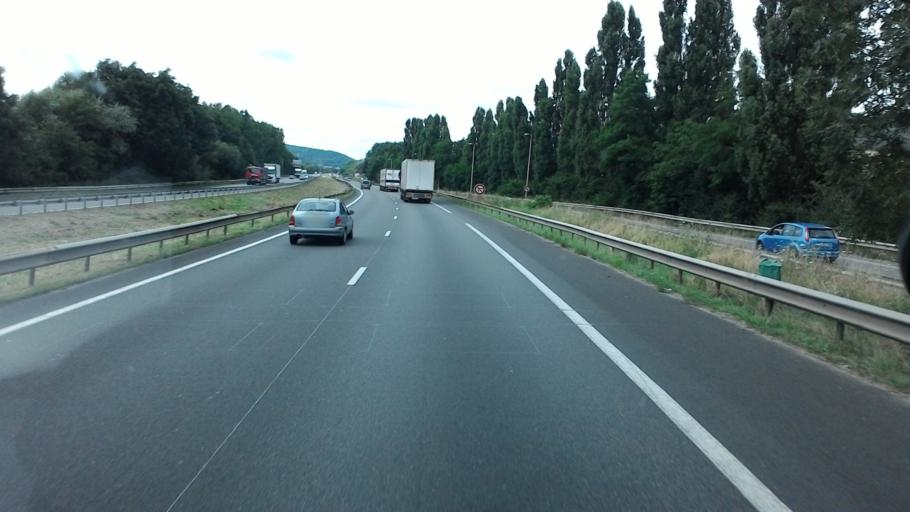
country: FR
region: Lorraine
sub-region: Departement de Meurthe-et-Moselle
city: Bouxieres-aux-Dames
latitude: 48.7540
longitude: 6.1562
